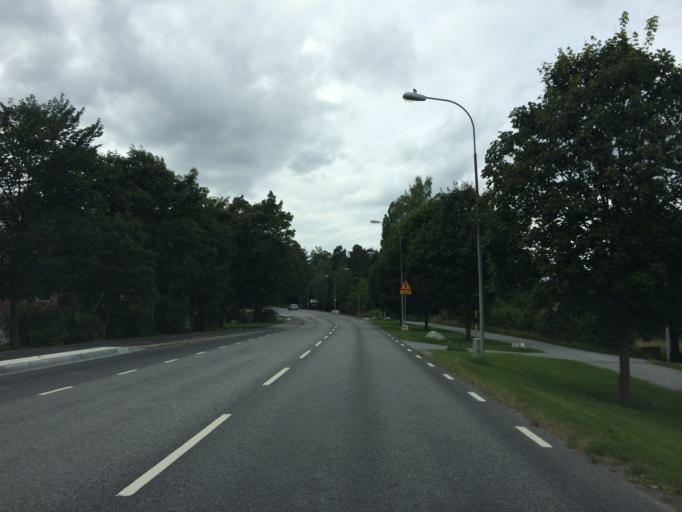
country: SE
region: Stockholm
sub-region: Sollentuna Kommun
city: Sollentuna
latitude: 59.4491
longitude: 17.9379
